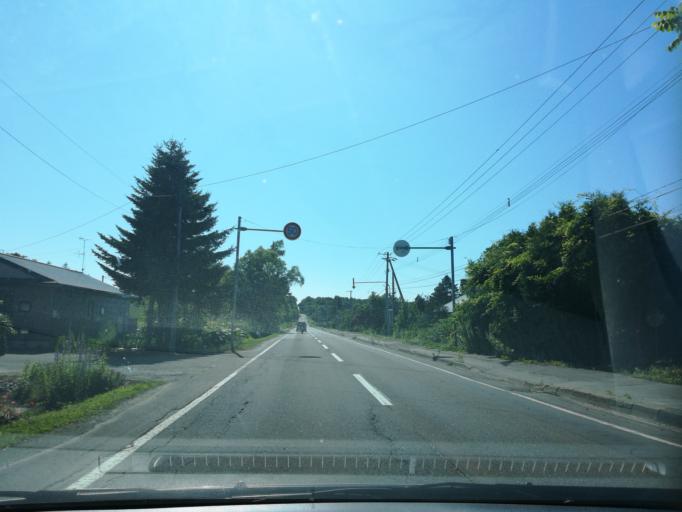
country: JP
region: Hokkaido
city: Chitose
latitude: 42.9147
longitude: 141.8880
